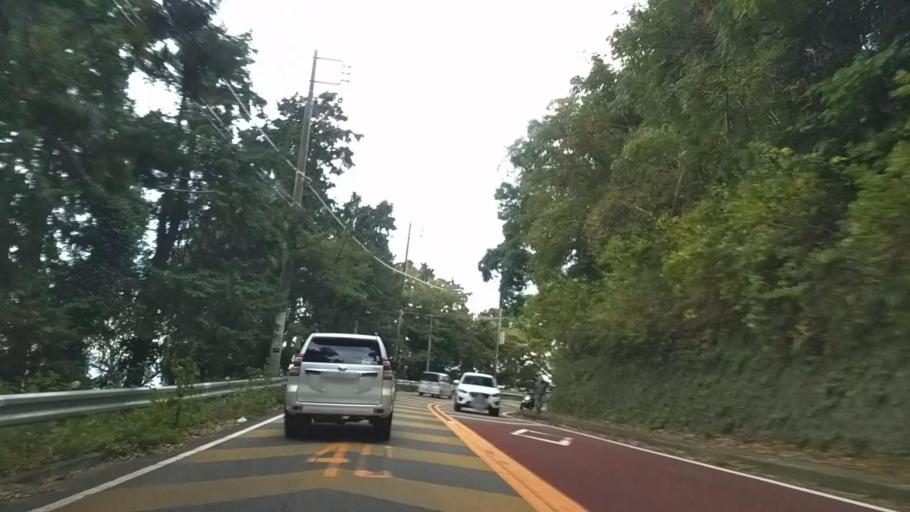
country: JP
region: Shizuoka
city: Atami
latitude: 35.1186
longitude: 139.0959
